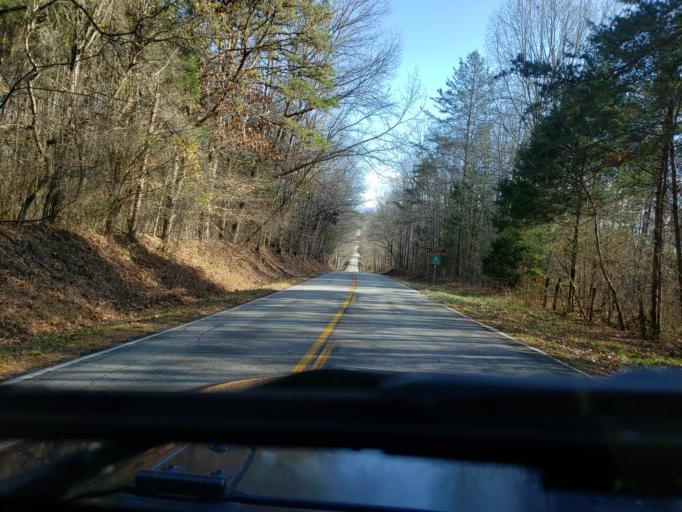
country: US
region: North Carolina
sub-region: Cleveland County
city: White Plains
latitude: 35.1588
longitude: -81.4041
